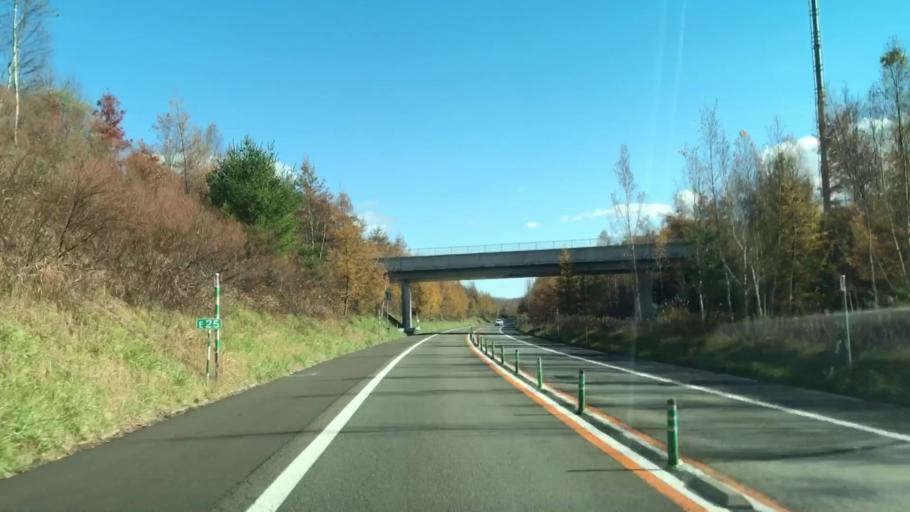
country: JP
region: Hokkaido
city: Chitose
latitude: 42.8985
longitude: 141.8528
